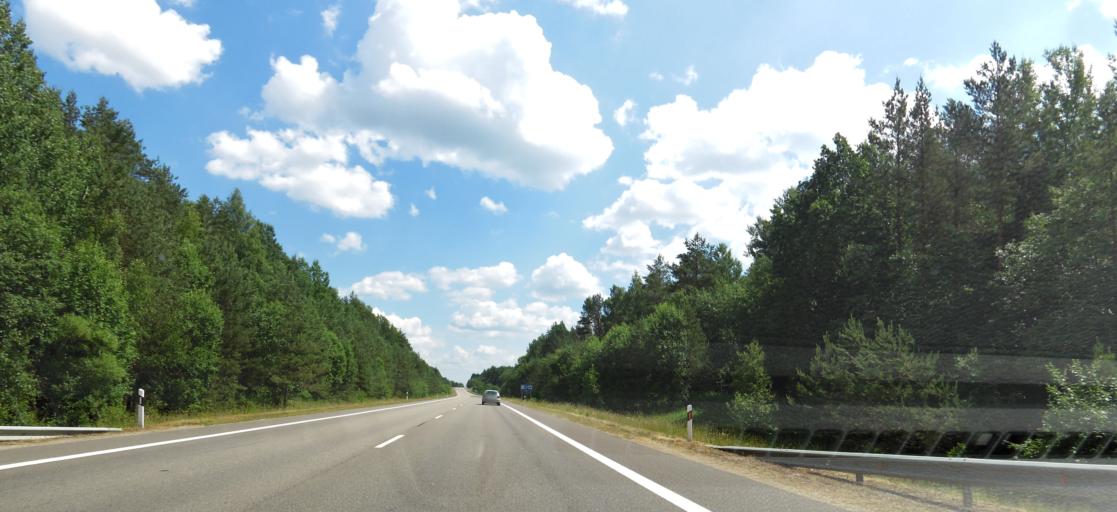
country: LT
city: Skaidiskes
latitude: 54.6141
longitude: 25.4306
